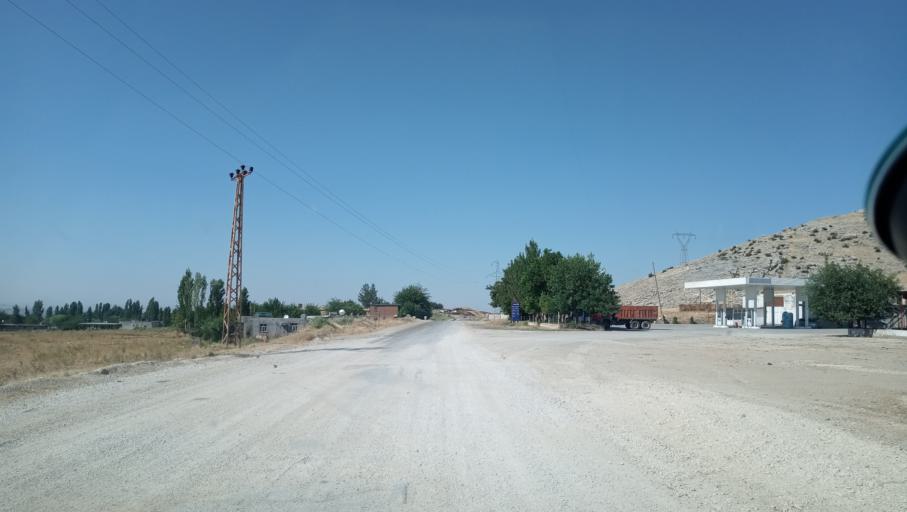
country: TR
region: Diyarbakir
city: Malabadi
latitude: 38.1379
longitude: 41.1919
